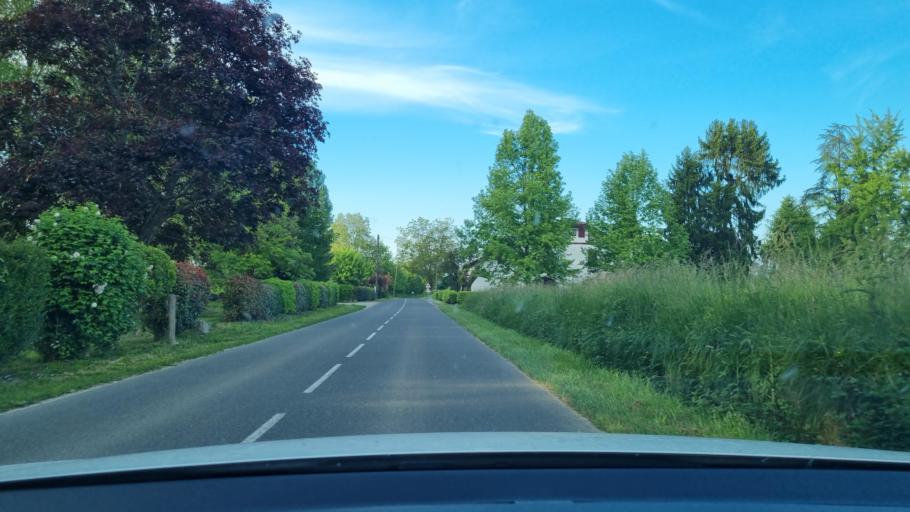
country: FR
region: Aquitaine
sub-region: Departement des Landes
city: Peyrehorade
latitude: 43.5393
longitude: -1.1425
